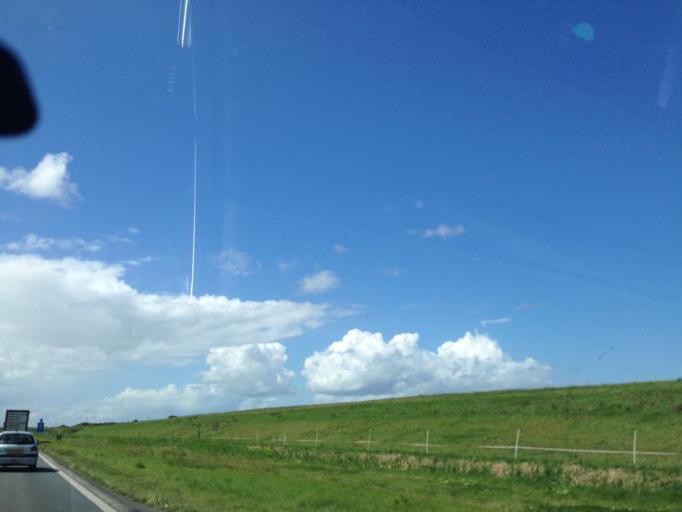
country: NL
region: Flevoland
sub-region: Gemeente Dronten
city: Dronten
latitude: 52.5492
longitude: 5.6448
